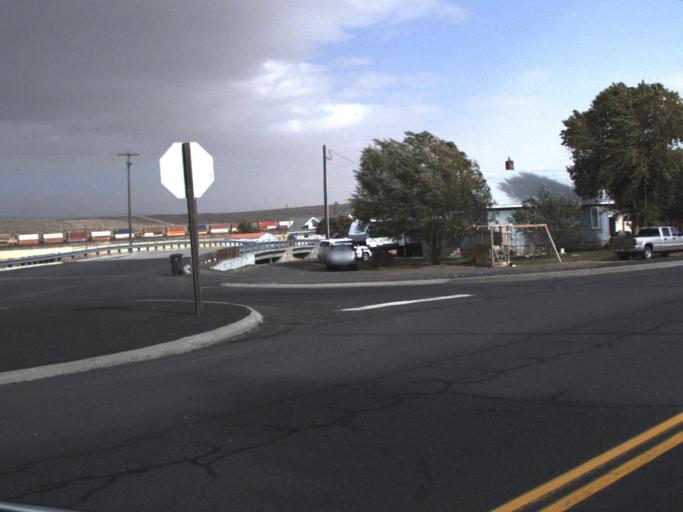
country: US
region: Washington
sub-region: Adams County
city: Ritzville
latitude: 47.3328
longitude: -118.6783
